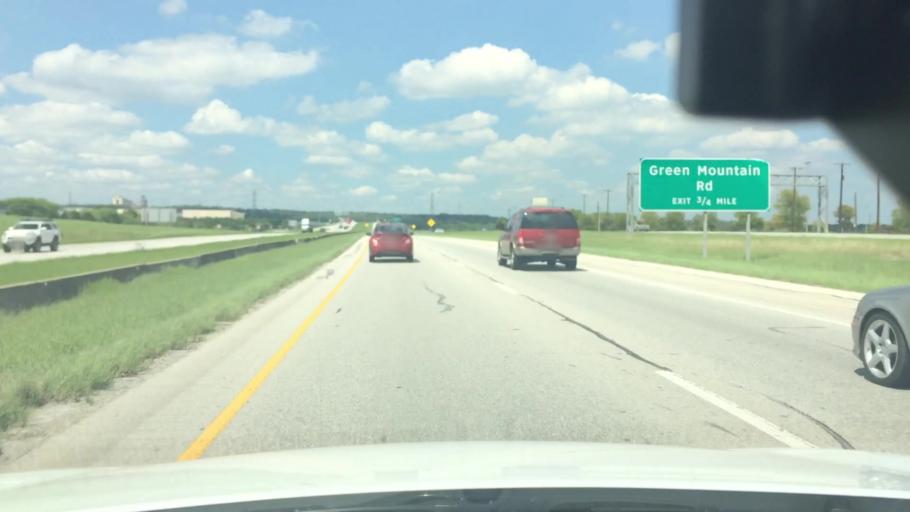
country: US
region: Texas
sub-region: Bexar County
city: Live Oak
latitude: 29.5938
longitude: -98.3535
